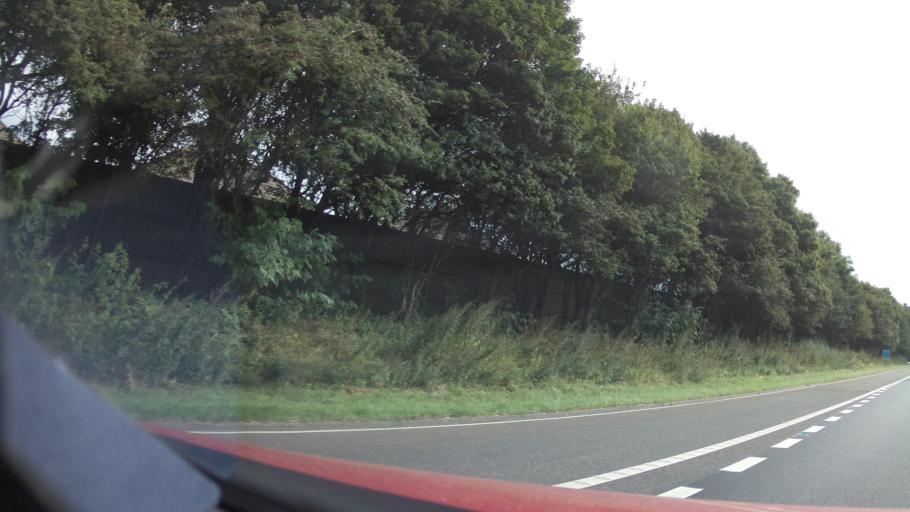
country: GB
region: England
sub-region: County Durham
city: West Rainton
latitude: 54.7887
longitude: -1.5313
